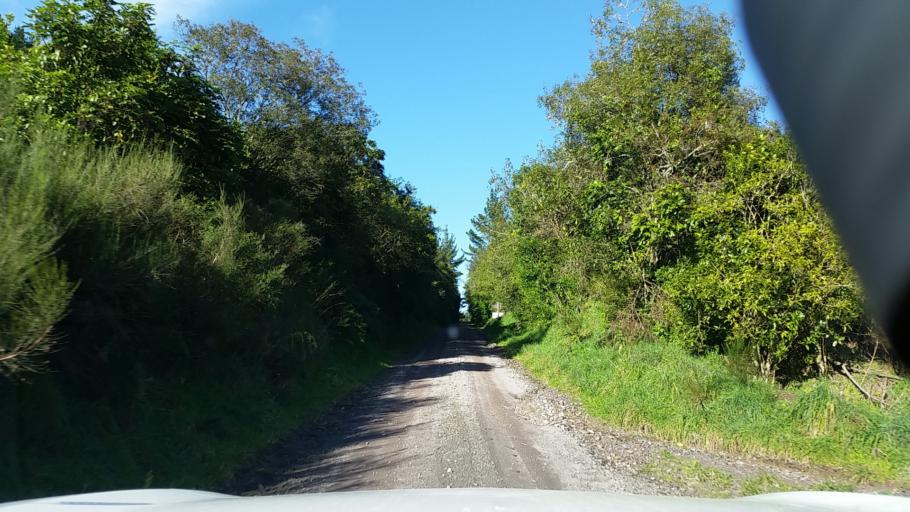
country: NZ
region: Waikato
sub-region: Taupo District
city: Taupo
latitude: -38.4069
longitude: 176.1400
